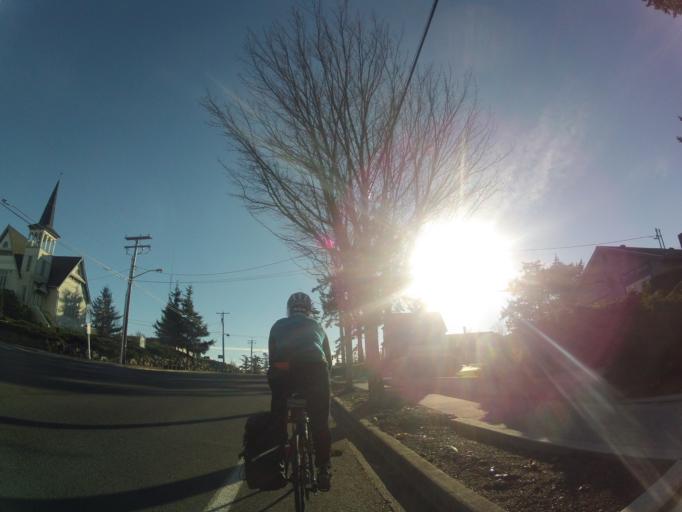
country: US
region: Washington
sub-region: Island County
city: Coupeville
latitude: 48.2158
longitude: -122.6862
